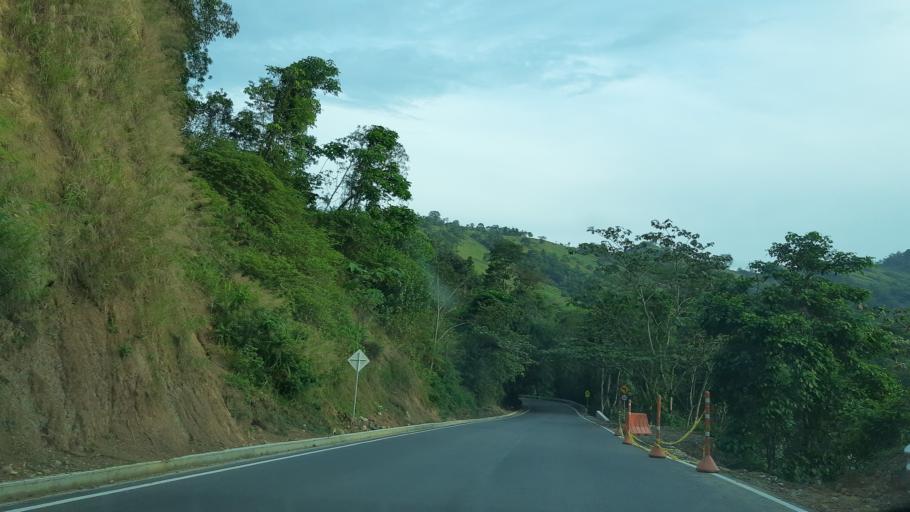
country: CO
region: Boyaca
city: San Luis de Gaceno
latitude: 4.8326
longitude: -73.1340
